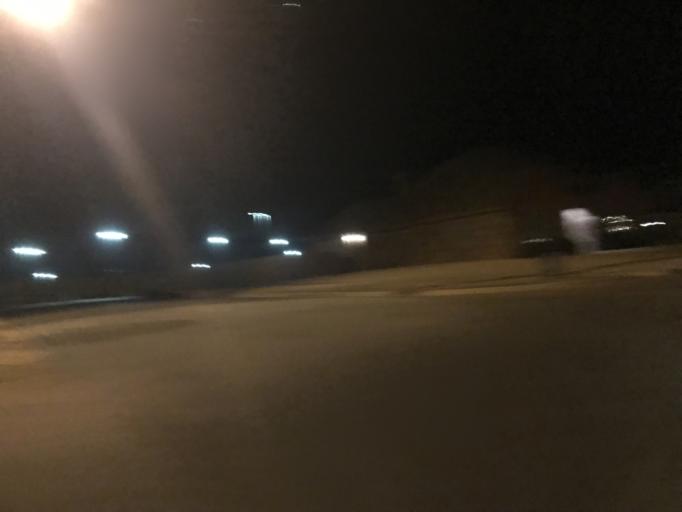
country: US
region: Texas
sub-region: Taylor County
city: Potosi
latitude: 32.3735
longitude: -99.7172
